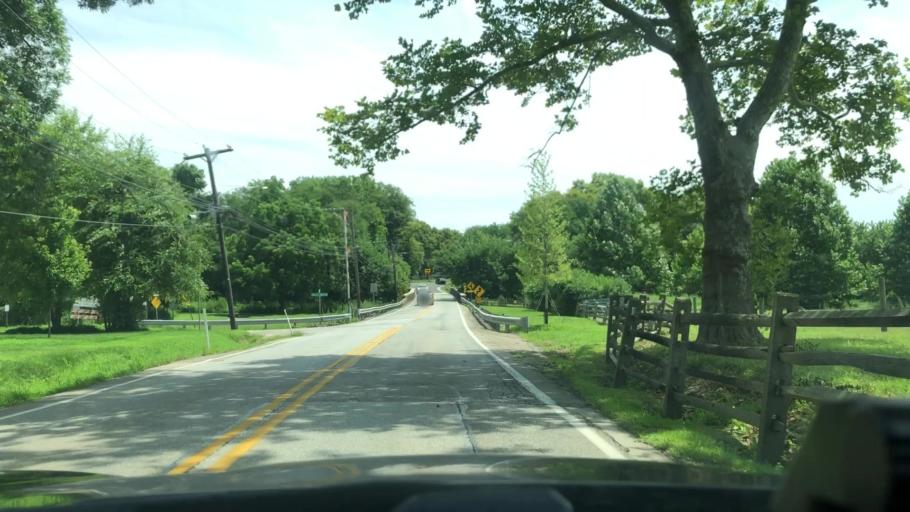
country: US
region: Pennsylvania
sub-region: Montgomery County
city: Flourtown
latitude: 40.1027
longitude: -75.2316
